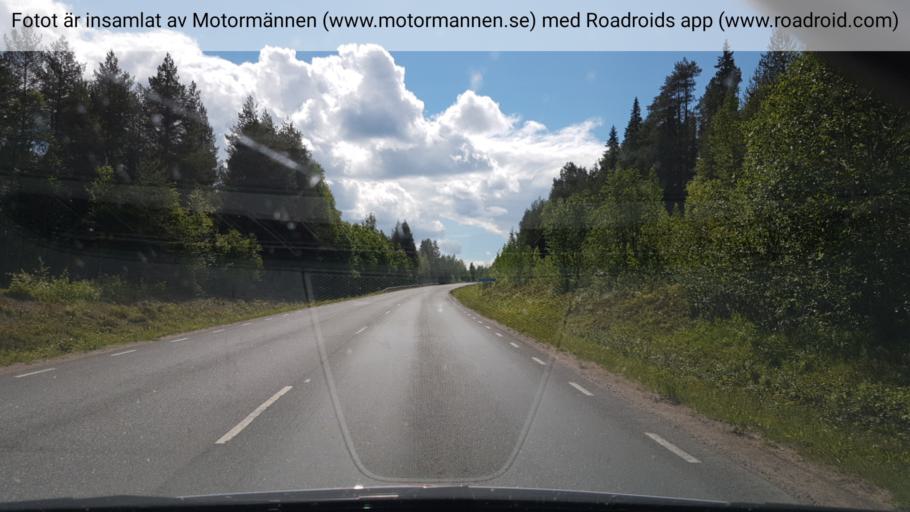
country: SE
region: Norrbotten
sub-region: Overtornea Kommun
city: OEvertornea
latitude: 66.3800
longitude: 23.6474
